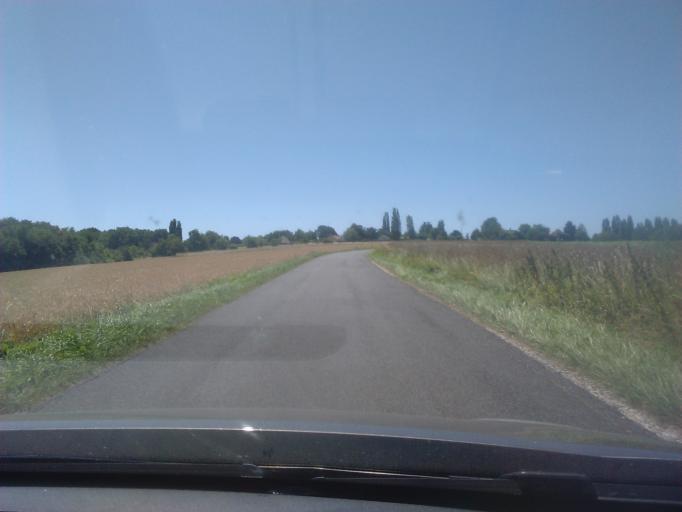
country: FR
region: Centre
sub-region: Departement du Loir-et-Cher
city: Saint-Sulpice-de-Pommeray
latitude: 47.6015
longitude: 1.2204
